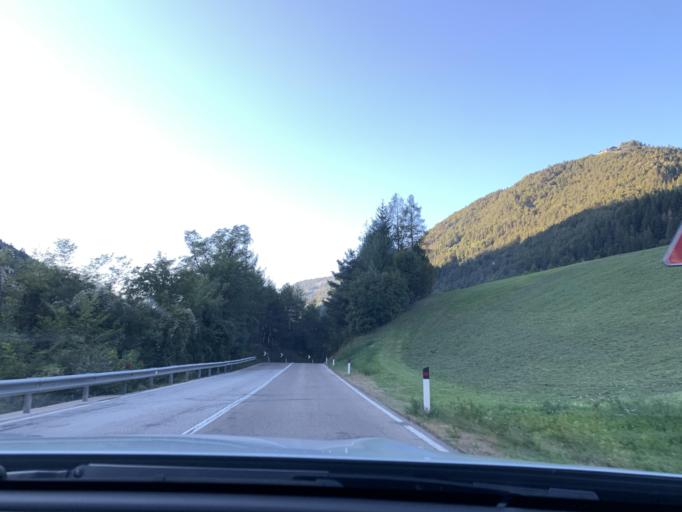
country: IT
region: Trentino-Alto Adige
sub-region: Bolzano
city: Nova Ponente
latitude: 46.4397
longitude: 11.4652
